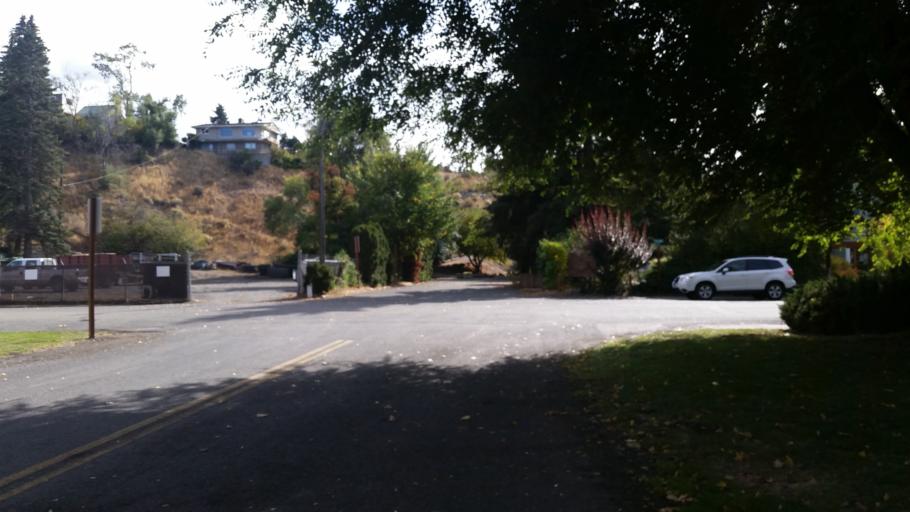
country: US
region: Washington
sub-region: Kittitas County
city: Ellensburg
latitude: 46.9970
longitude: -120.5354
